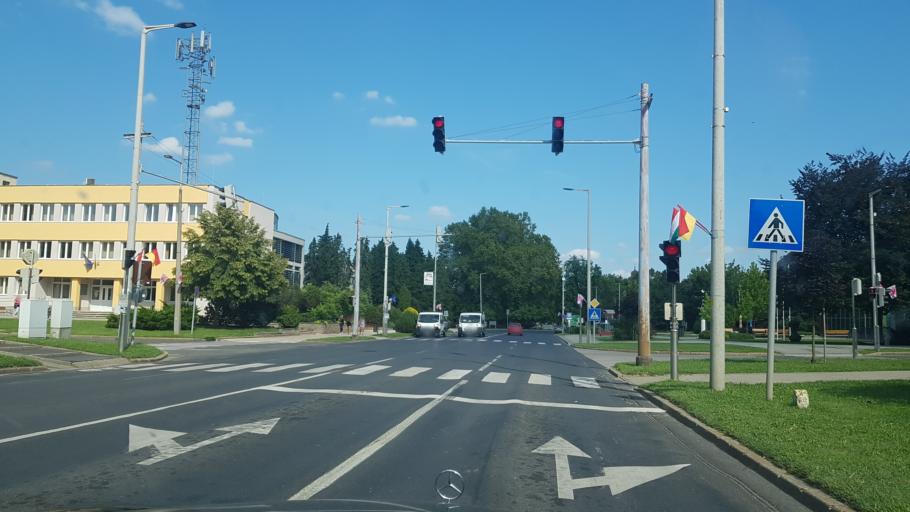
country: HU
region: Somogy
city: Nagyatad
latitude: 46.2297
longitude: 17.3609
